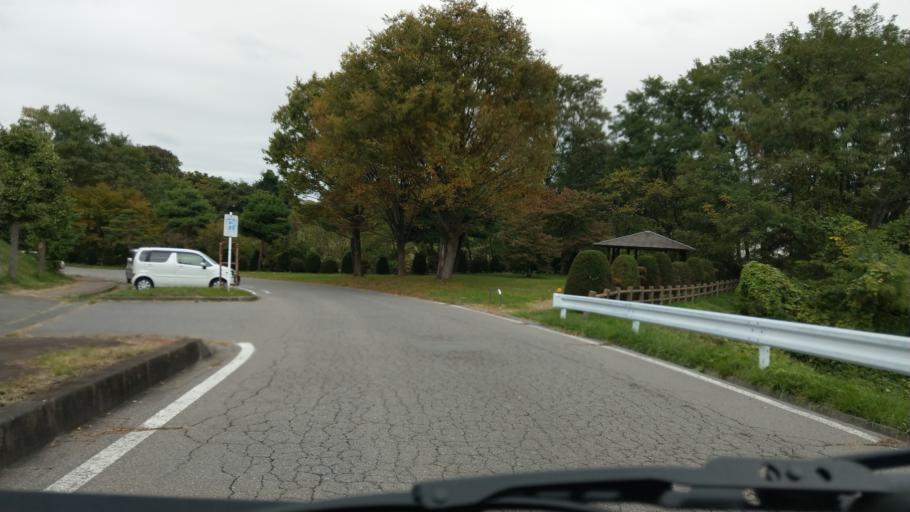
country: JP
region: Nagano
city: Komoro
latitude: 36.3111
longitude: 138.4361
